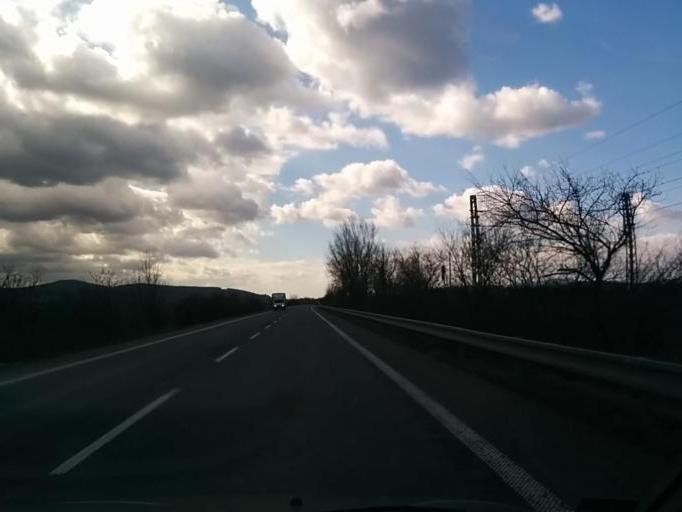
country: SK
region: Trenciansky
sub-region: Okres Trencin
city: Trencin
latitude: 48.8534
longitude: 17.9445
